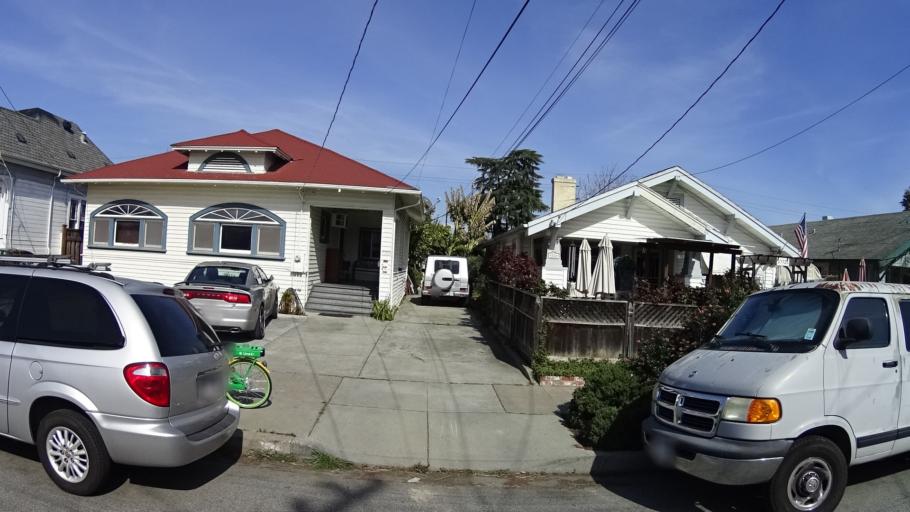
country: US
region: California
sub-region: Santa Clara County
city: San Jose
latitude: 37.3453
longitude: -121.8859
